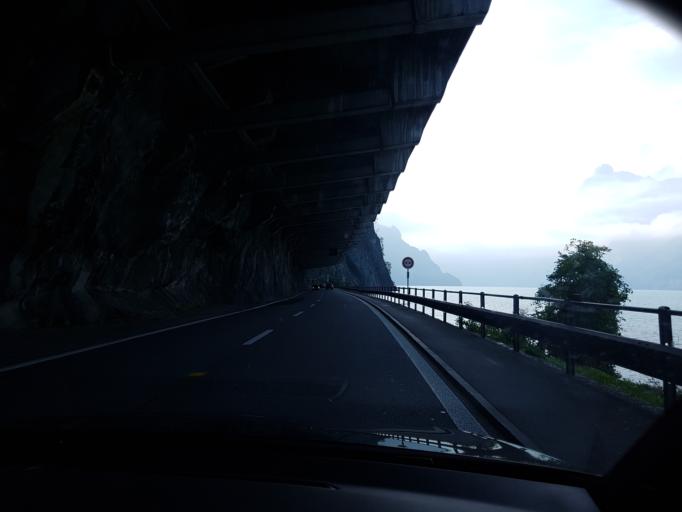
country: CH
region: Schwyz
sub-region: Bezirk Schwyz
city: Ingenbohl
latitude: 46.9627
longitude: 8.6144
